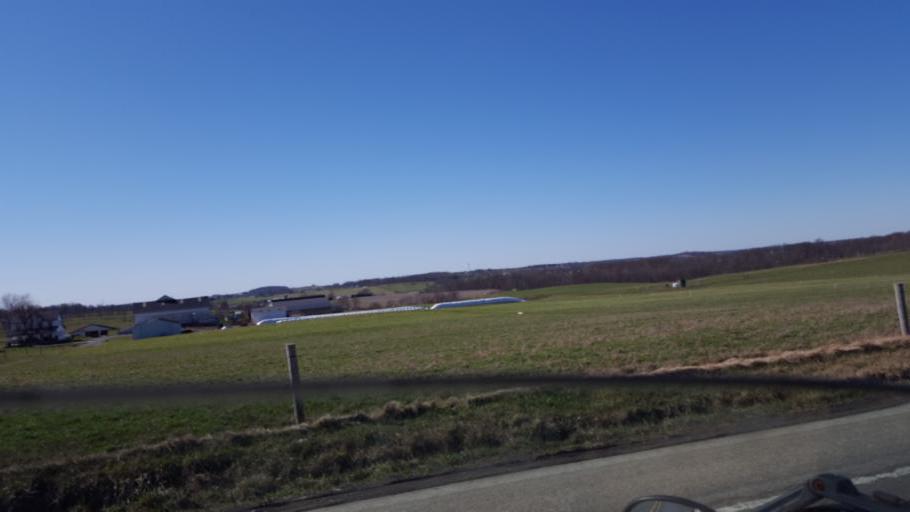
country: US
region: Ohio
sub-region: Wayne County
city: Apple Creek
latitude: 40.6352
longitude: -81.7844
